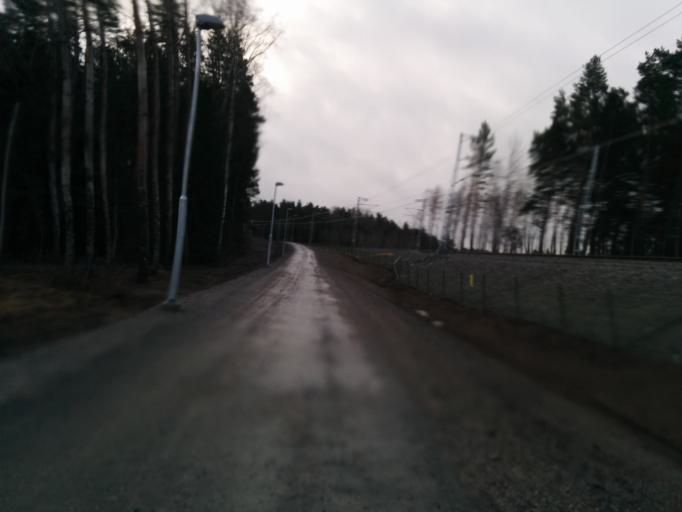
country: SE
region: Stockholm
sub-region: Taby Kommun
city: Taby
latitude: 59.4709
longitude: 18.0573
